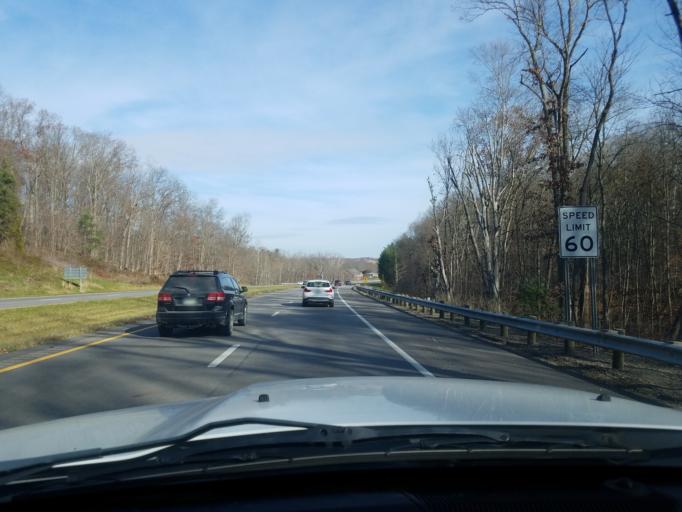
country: US
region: Ohio
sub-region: Athens County
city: Athens
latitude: 39.2840
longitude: -82.1493
